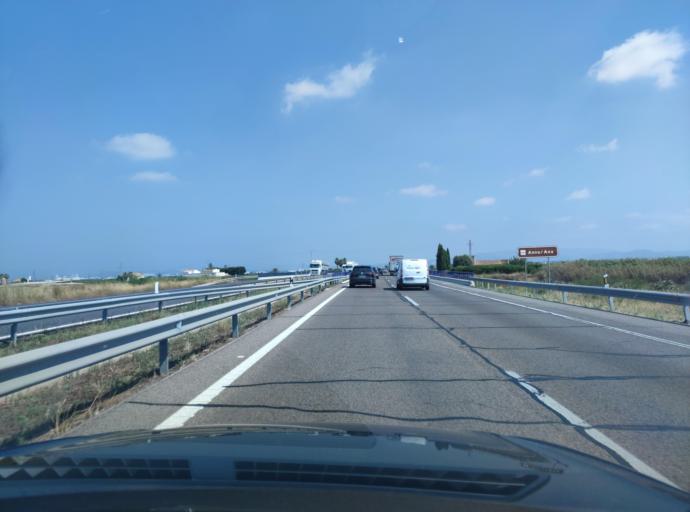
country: ES
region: Valencia
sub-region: Provincia de Castello
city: Alquerias del Nino Perdido
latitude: 39.9087
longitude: -0.1351
